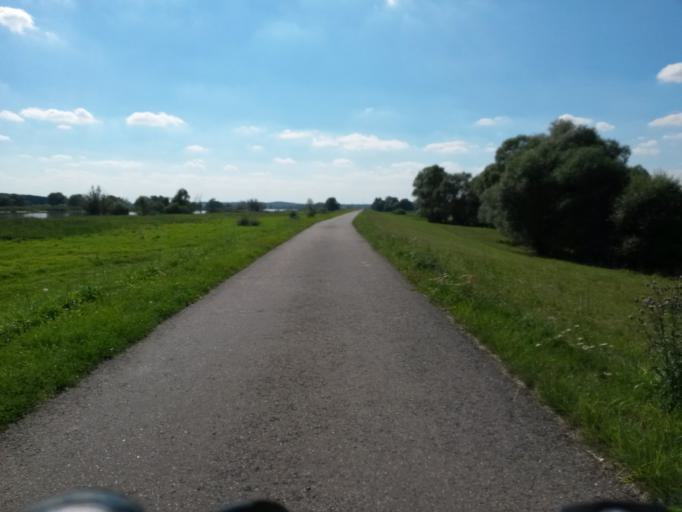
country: DE
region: Brandenburg
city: Schoneberg
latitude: 52.9822
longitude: 14.1887
